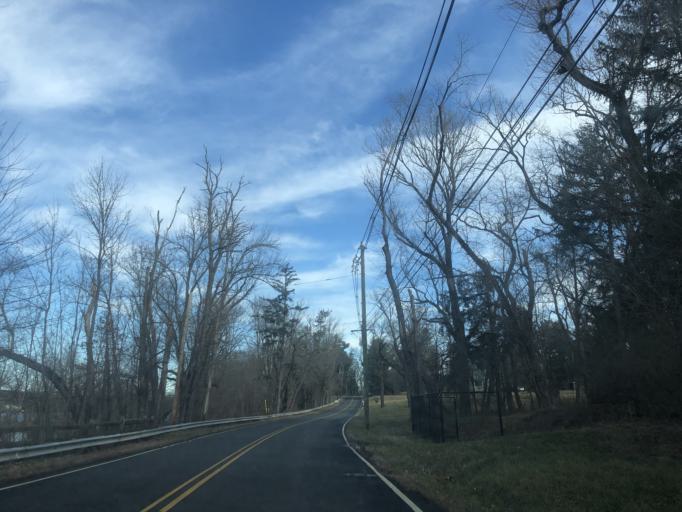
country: US
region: New Jersey
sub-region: Somerset County
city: Kingston
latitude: 40.3559
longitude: -74.6247
